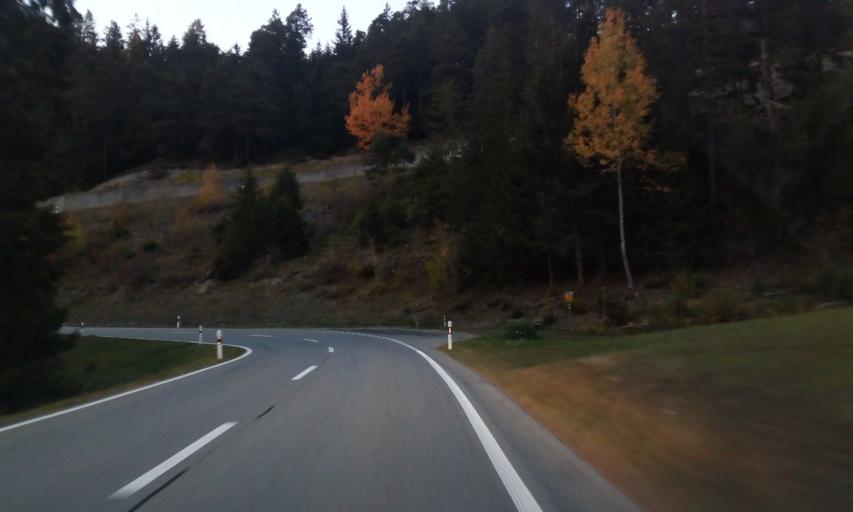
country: CH
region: Grisons
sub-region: Albula District
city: Tiefencastel
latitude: 46.6685
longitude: 9.6268
